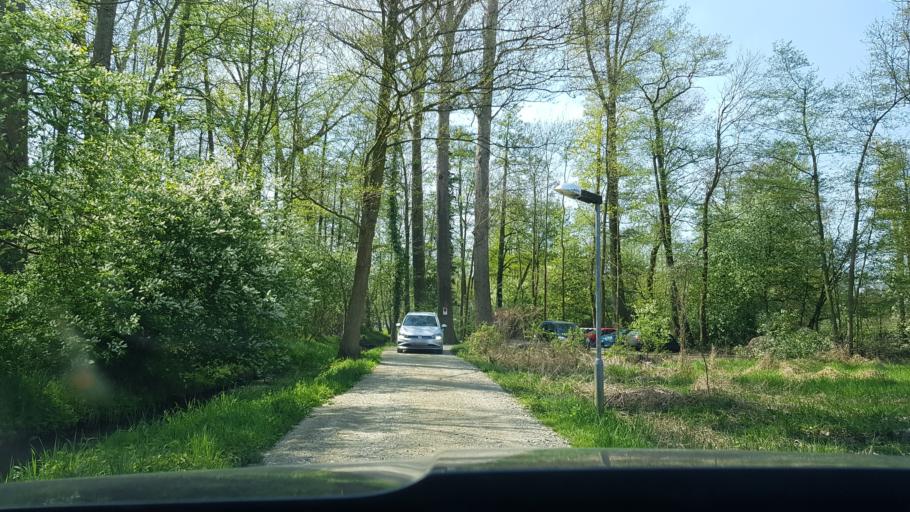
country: DE
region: Brandenburg
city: Lubbenau
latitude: 51.8656
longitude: 13.9867
